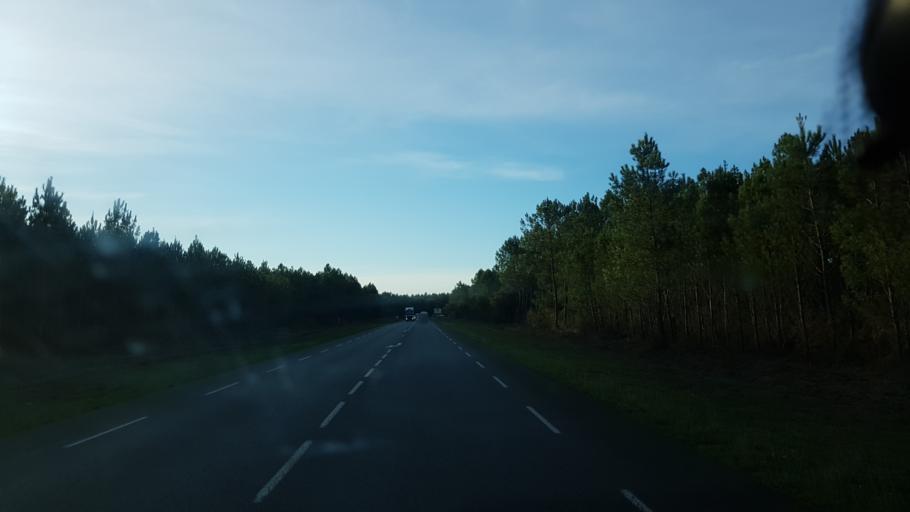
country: FR
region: Aquitaine
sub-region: Departement de la Gironde
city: Martignas-sur-Jalle
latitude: 44.8329
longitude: -0.7976
